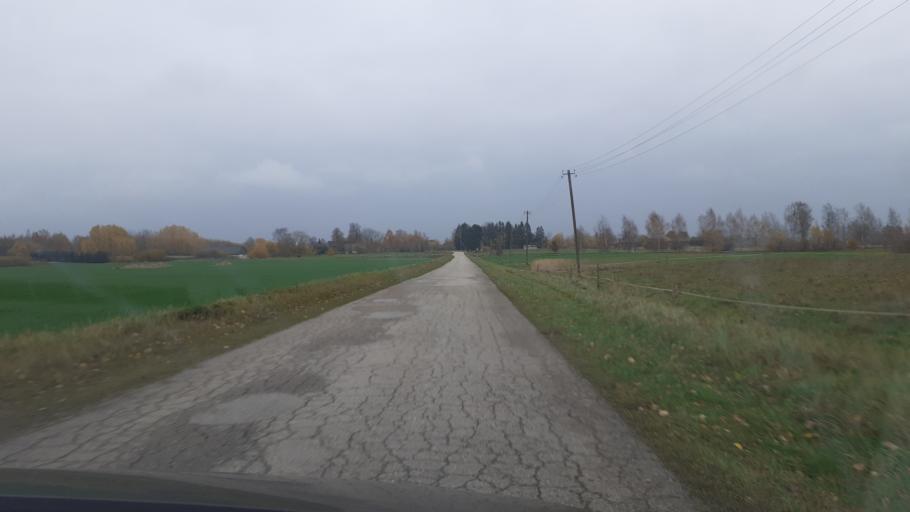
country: LV
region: Skrunda
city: Skrunda
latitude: 56.8588
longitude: 22.2576
